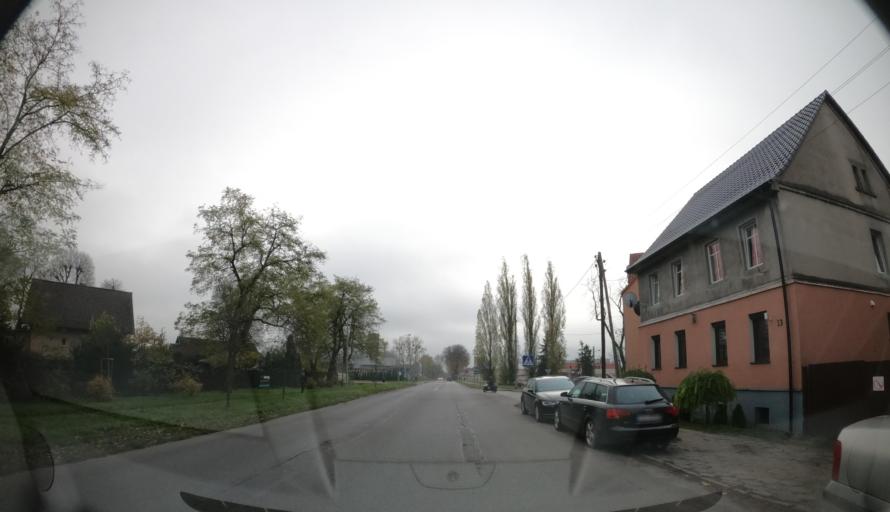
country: PL
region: West Pomeranian Voivodeship
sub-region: Powiat goleniowski
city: Goleniow
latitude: 53.5721
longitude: 14.8311
